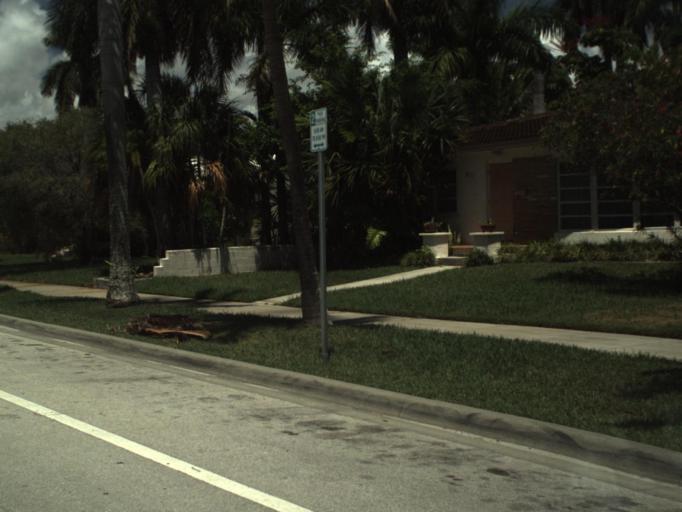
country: US
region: Florida
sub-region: Broward County
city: Hollywood
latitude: 26.0122
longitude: -80.1210
